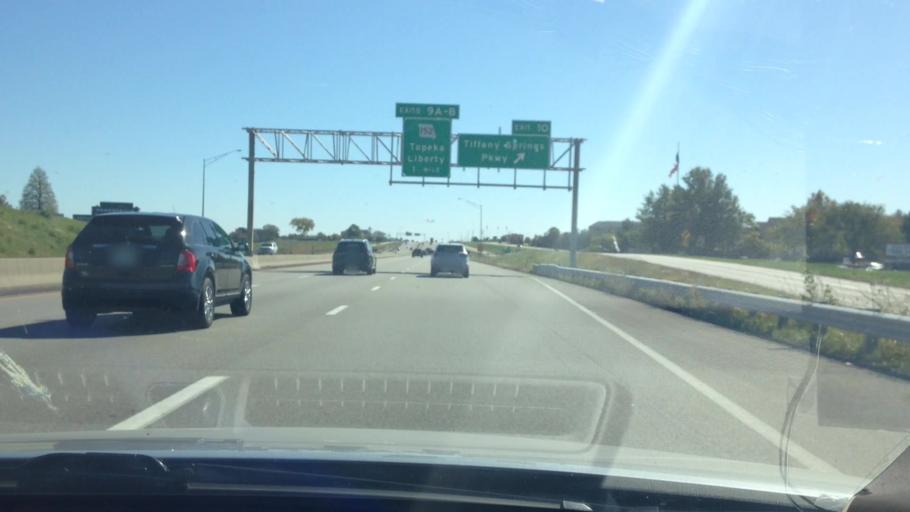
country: US
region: Missouri
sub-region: Platte County
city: Weatherby Lake
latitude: 39.2776
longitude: -94.6726
